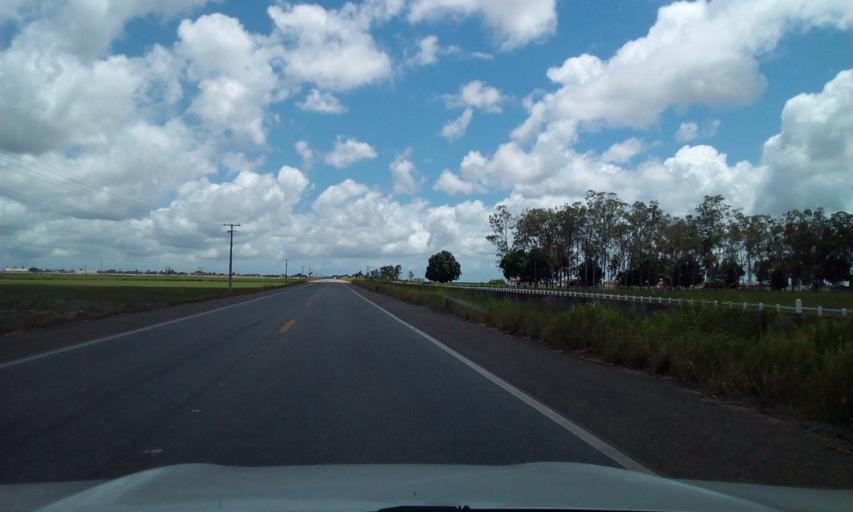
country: BR
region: Alagoas
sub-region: Campo Alegre
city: Campo Alegre
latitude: -9.9018
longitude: -36.2380
